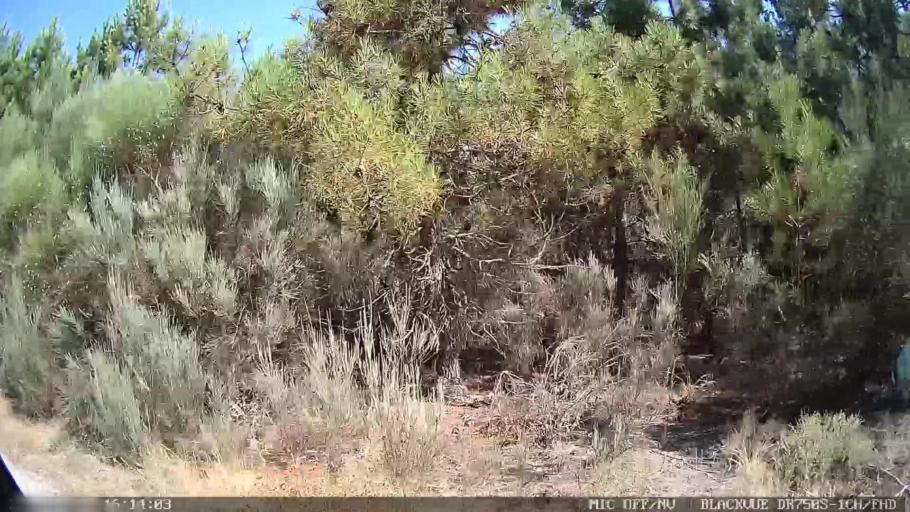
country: PT
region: Vila Real
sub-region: Murca
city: Murca
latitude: 41.3373
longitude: -7.4783
